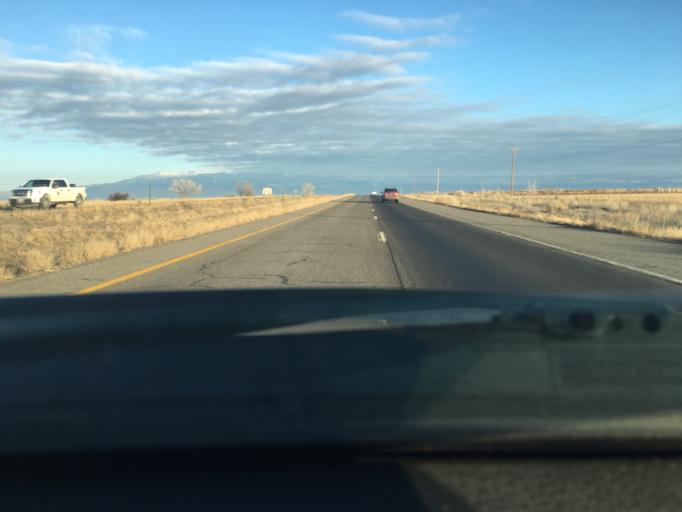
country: US
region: Colorado
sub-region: Montrose County
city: Olathe
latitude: 38.6372
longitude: -107.9870
